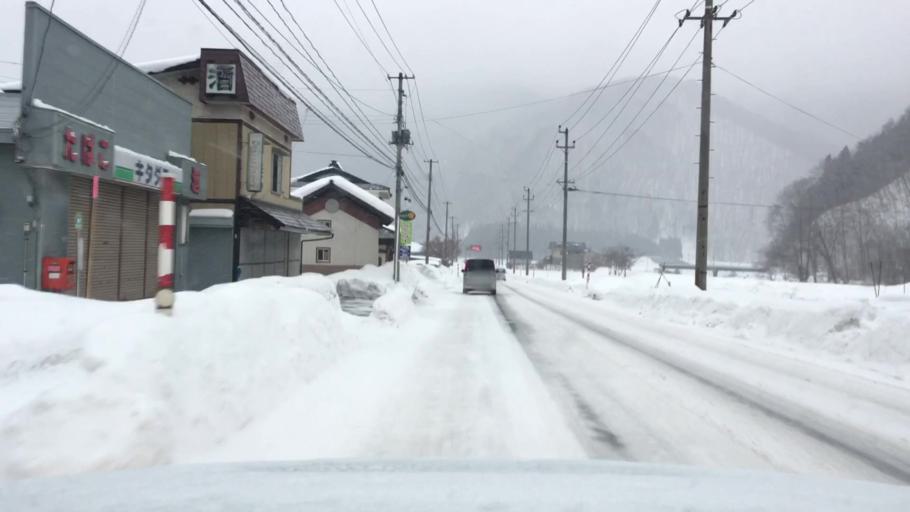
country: JP
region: Akita
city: Hanawa
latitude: 40.0764
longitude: 141.0213
